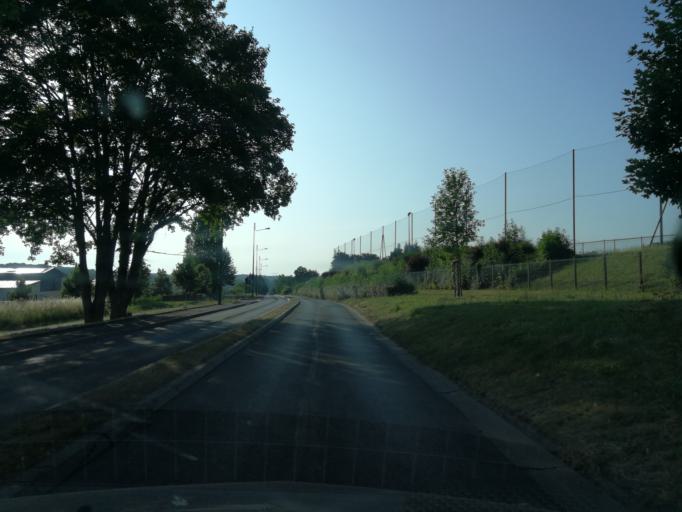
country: FR
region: Ile-de-France
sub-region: Departement de l'Essonne
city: Limours
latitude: 48.6428
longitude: 2.0848
